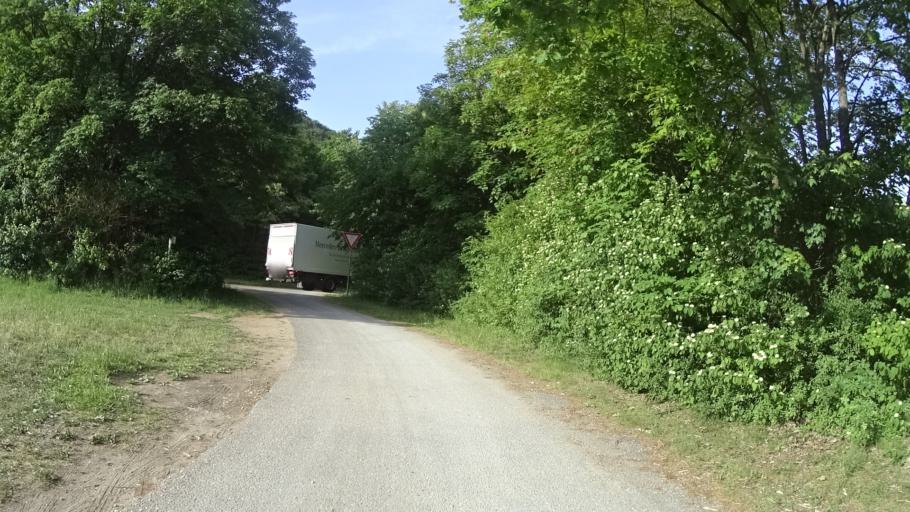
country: DE
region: Bavaria
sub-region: Lower Bavaria
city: Riedenburg
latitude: 48.9751
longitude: 11.6898
